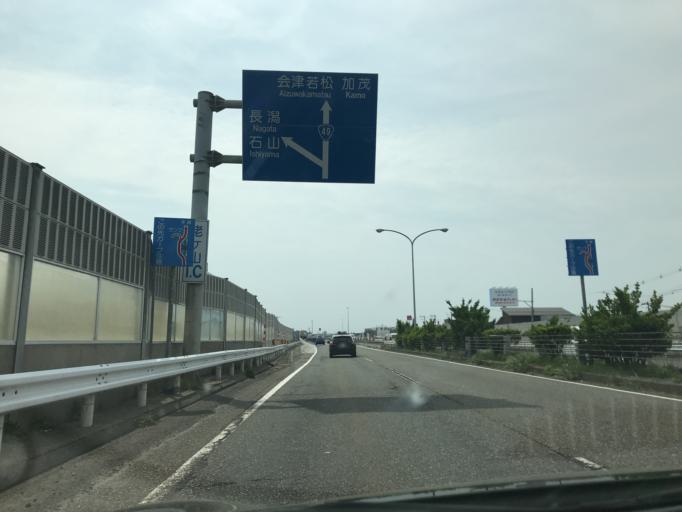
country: JP
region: Niigata
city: Kameda-honcho
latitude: 37.8862
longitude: 139.0782
